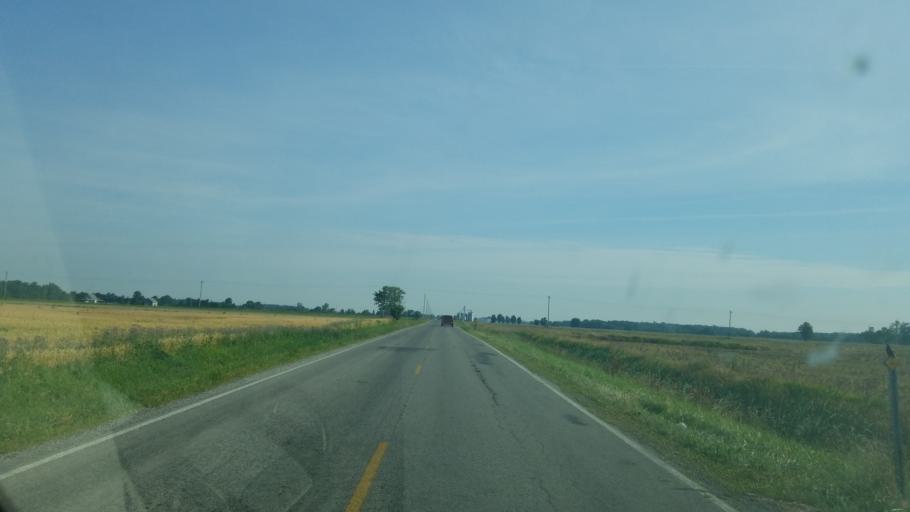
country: US
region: Ohio
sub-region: Hancock County
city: Arlington
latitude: 40.9630
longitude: -83.6985
